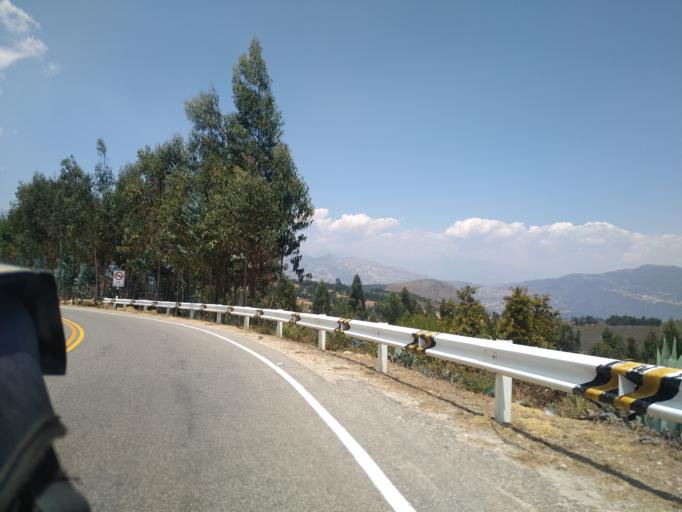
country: PE
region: Cajamarca
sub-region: San Marcos
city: San Marcos
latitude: -7.2861
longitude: -78.2135
